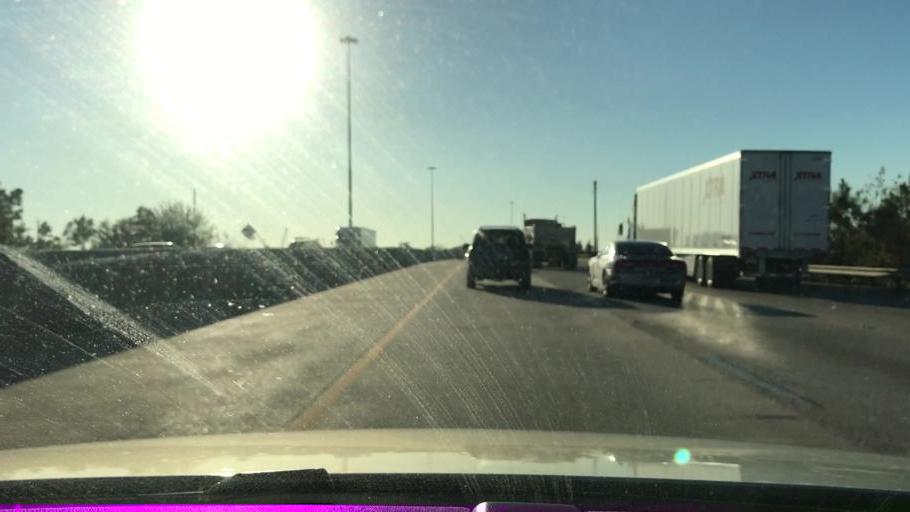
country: US
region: Texas
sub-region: Harris County
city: Highlands
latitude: 29.7929
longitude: -95.0782
